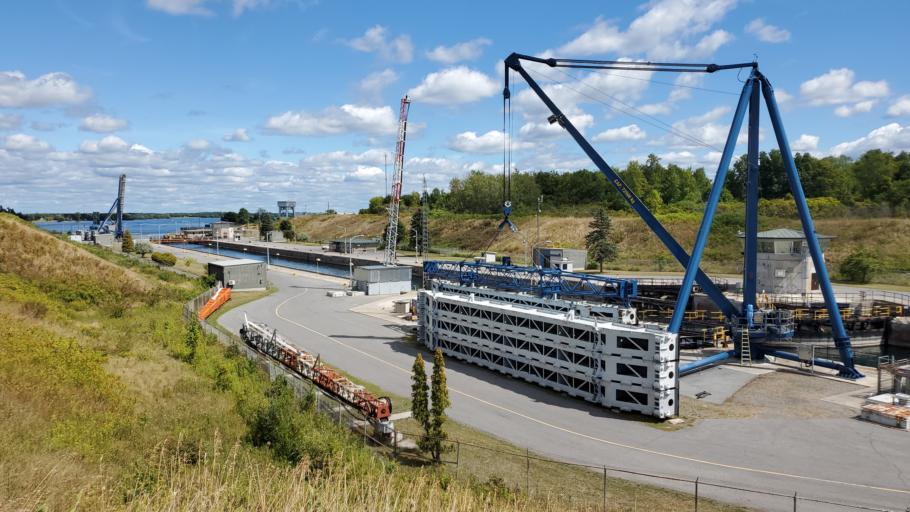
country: US
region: New York
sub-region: St. Lawrence County
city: Ogdensburg
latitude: 44.8294
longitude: -75.3145
